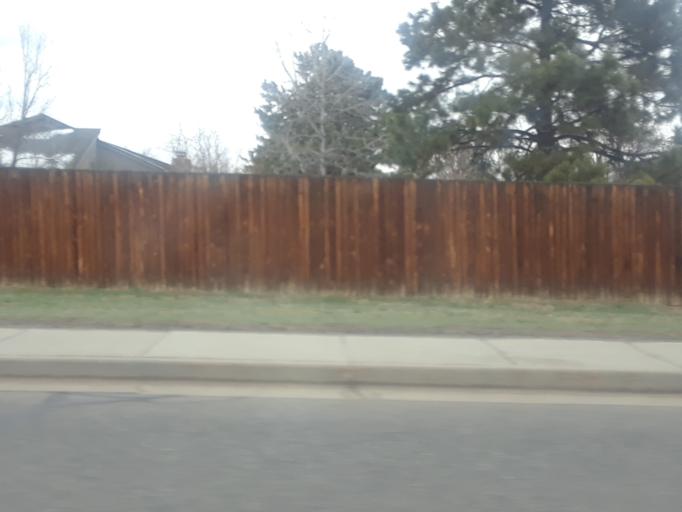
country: US
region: Colorado
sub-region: Douglas County
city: Acres Green
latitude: 39.5661
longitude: -104.8932
